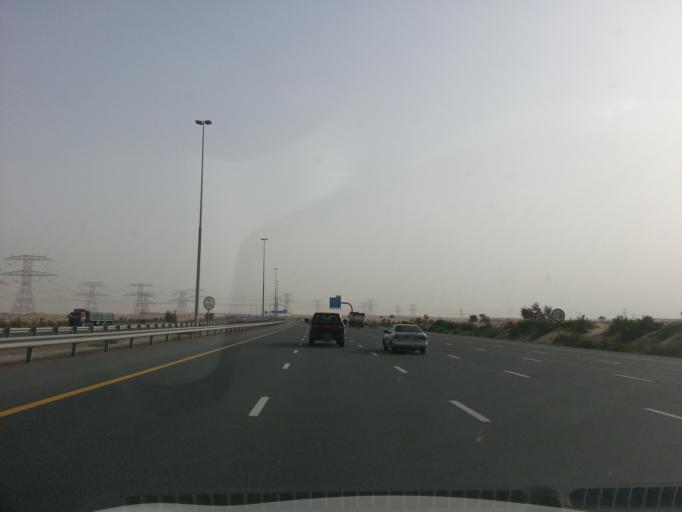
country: AE
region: Dubai
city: Dubai
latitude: 24.9921
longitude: 55.2491
